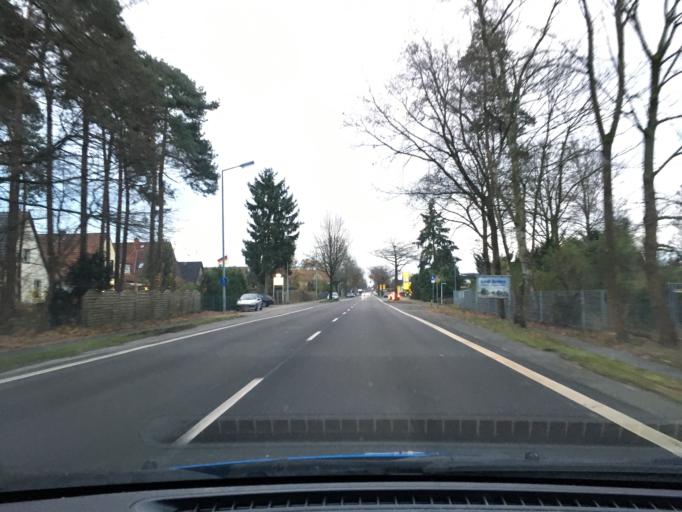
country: DE
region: Lower Saxony
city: Celle
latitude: 52.6581
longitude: 10.0547
